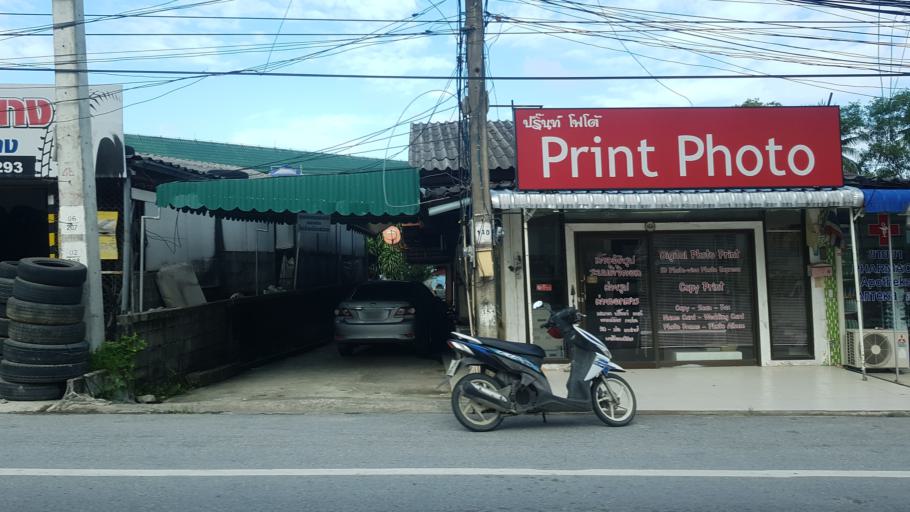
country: TH
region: Surat Thani
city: Ko Samui
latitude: 9.5346
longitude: 100.0421
